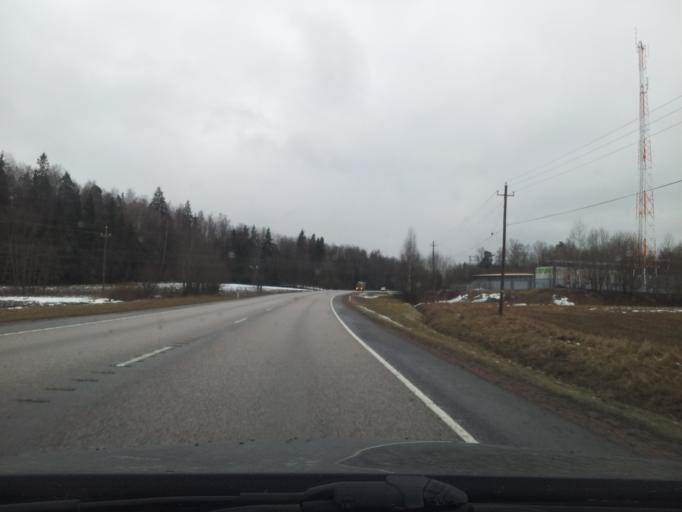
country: FI
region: Uusimaa
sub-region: Helsinki
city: Kirkkonummi
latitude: 60.1495
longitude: 24.5421
